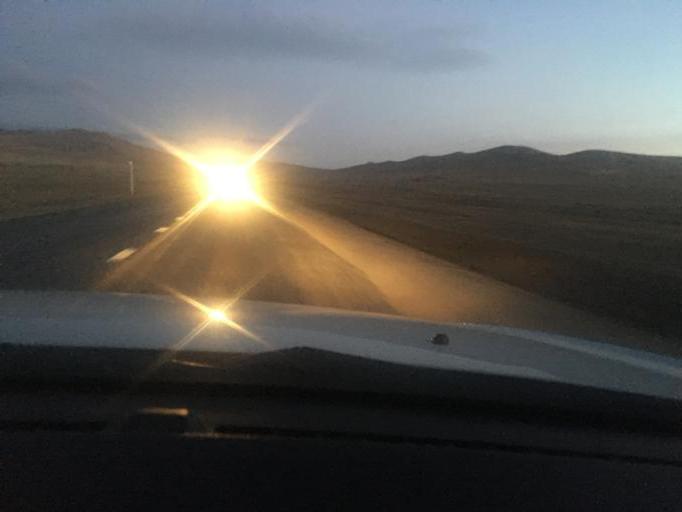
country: MN
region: Ulaanbaatar
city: Ulaanbaatar
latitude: 47.9865
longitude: 106.5637
